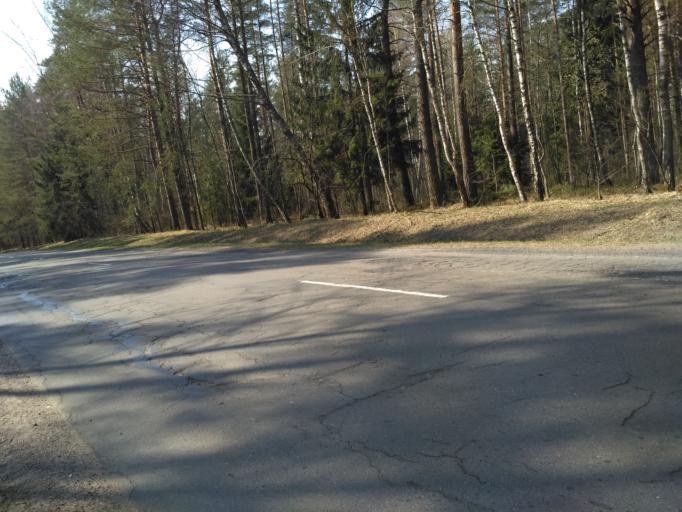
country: BY
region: Minsk
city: Zamostochcha
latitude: 53.9006
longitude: 27.9294
